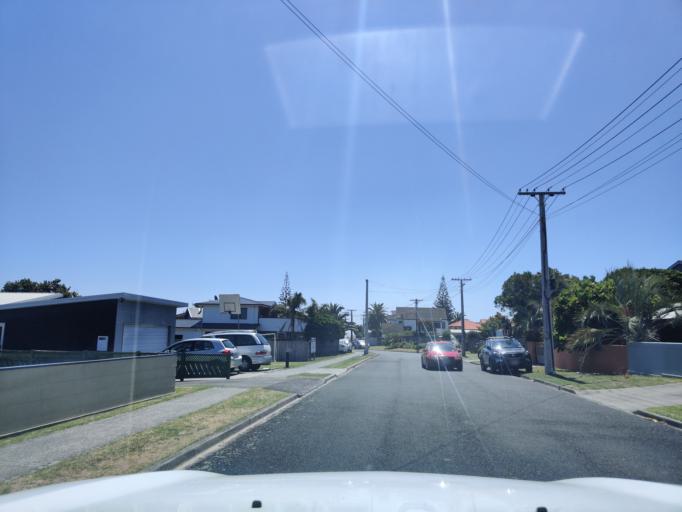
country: NZ
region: Bay of Plenty
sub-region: Western Bay of Plenty District
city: Maketu
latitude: -37.7136
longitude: 176.3348
